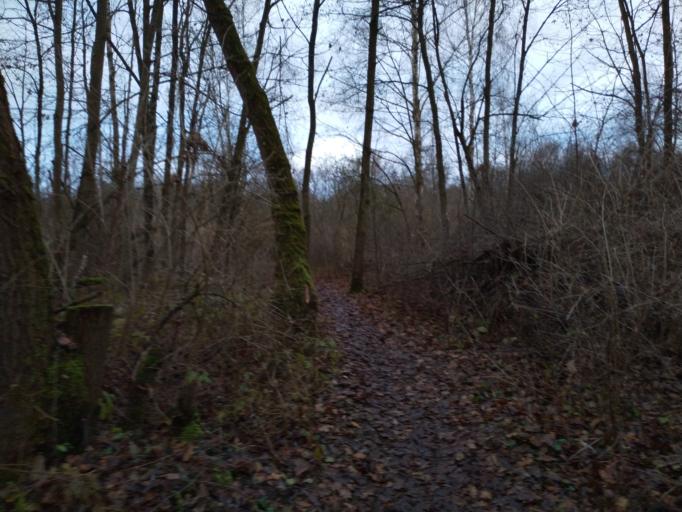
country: DE
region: Bavaria
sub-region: Swabia
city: Guenzburg
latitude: 48.4758
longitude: 10.3098
